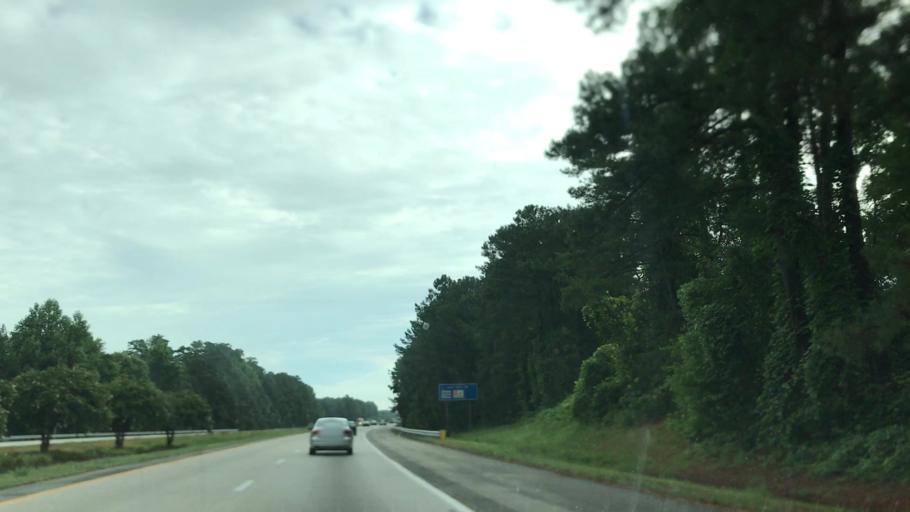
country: US
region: North Carolina
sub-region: Nash County
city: Red Oak
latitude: 36.0063
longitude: -77.8678
